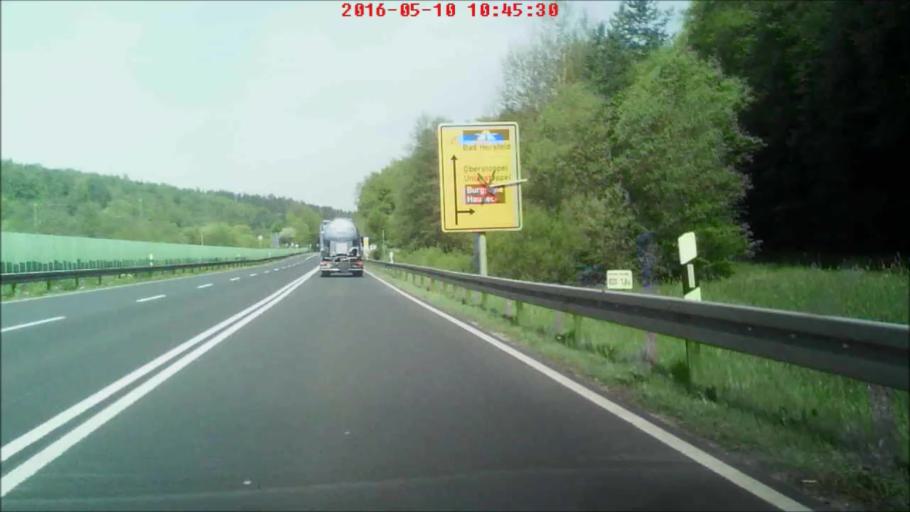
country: DE
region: Hesse
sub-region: Regierungsbezirk Kassel
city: Burghaun
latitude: 50.7326
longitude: 9.6974
